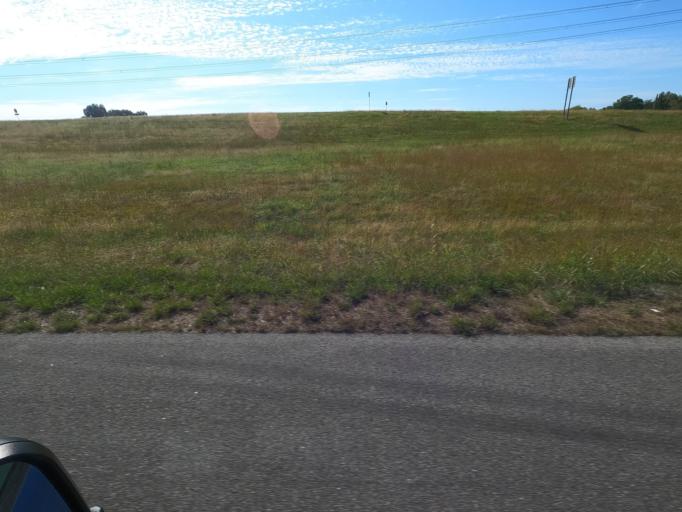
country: US
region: Tennessee
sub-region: Shelby County
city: Arlington
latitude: 35.3114
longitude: -89.7299
